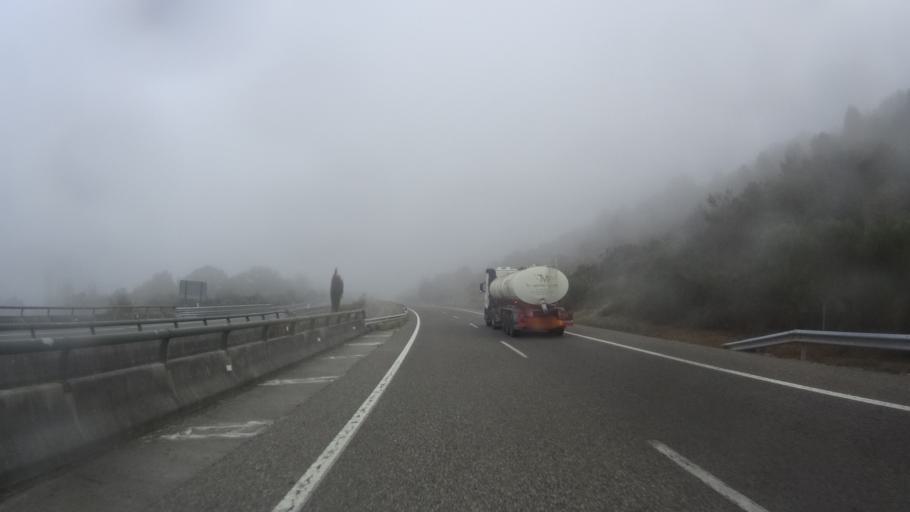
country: ES
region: Galicia
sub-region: Provincia de Lugo
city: Becerrea
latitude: 42.8195
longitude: -7.1086
